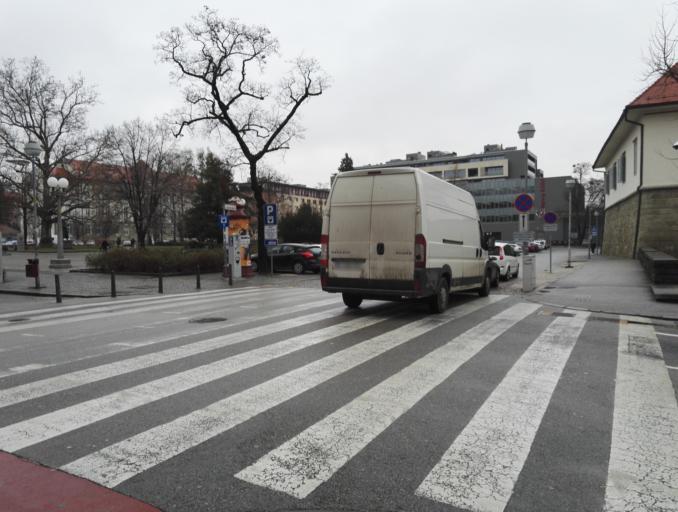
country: SI
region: Maribor
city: Maribor
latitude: 46.5611
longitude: 15.6482
